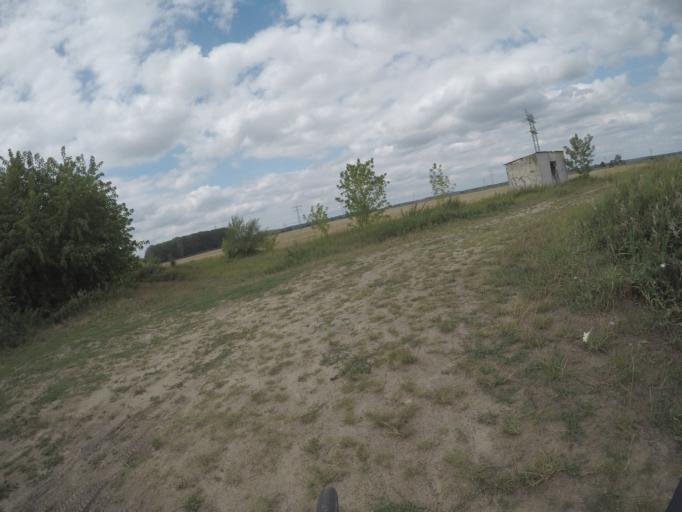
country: DE
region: Brandenburg
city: Falkensee
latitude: 52.6073
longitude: 13.0613
